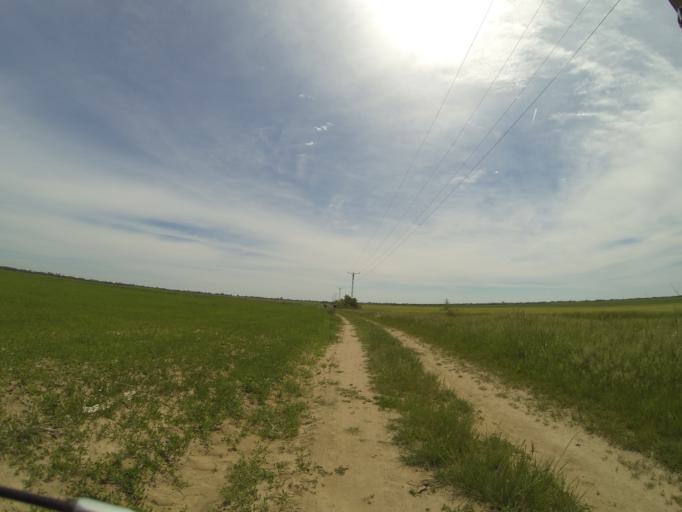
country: RO
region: Dolj
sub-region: Comuna Ghindeni
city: Ghindeni
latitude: 44.2057
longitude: 23.9587
